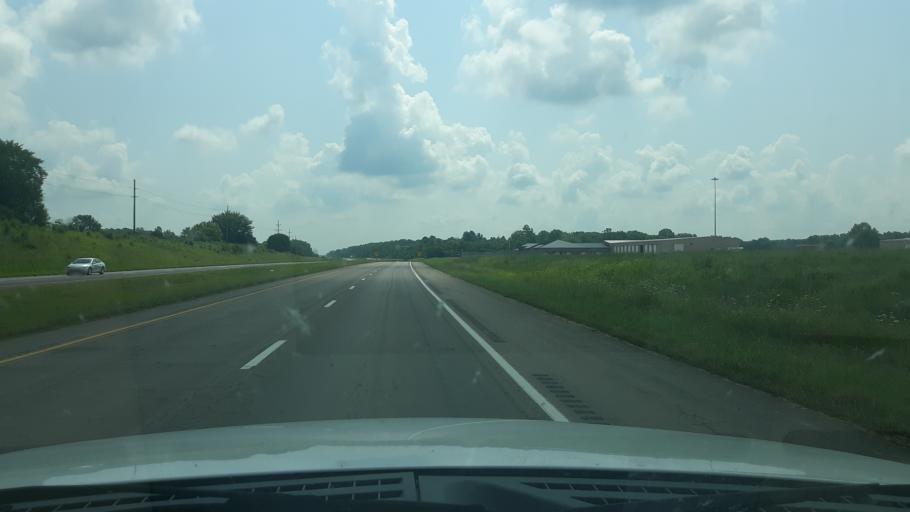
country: US
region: Illinois
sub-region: Saline County
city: Carrier Mills
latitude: 37.7337
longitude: -88.6793
